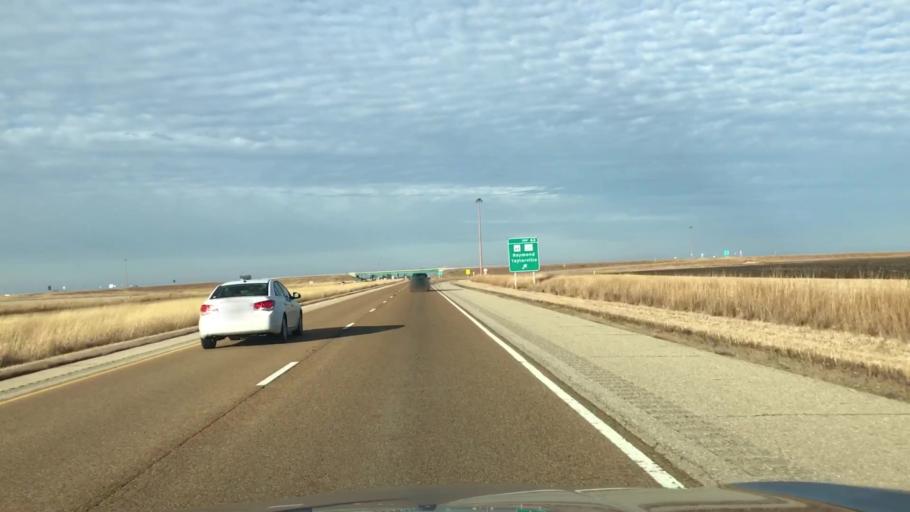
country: US
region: Illinois
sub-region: Montgomery County
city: Raymond
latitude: 39.3157
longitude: -89.6423
